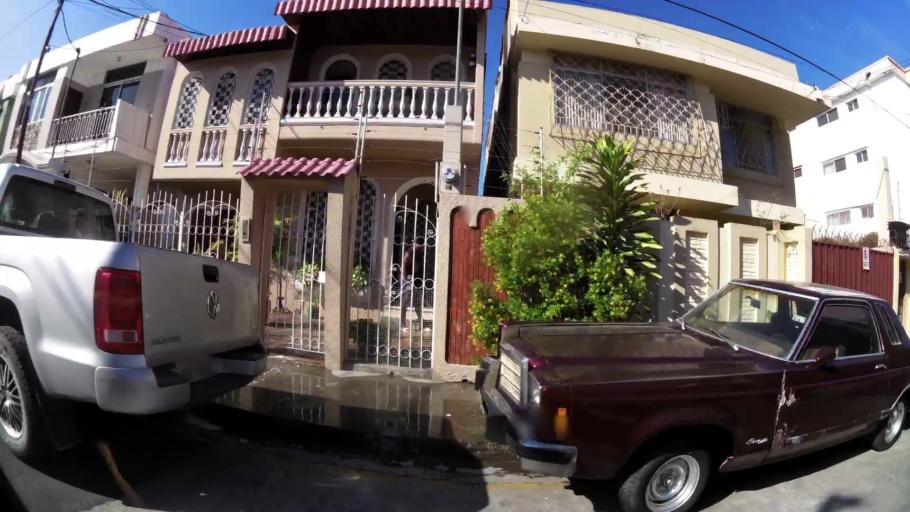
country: EC
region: Guayas
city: Guayaquil
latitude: -2.1738
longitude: -79.8971
